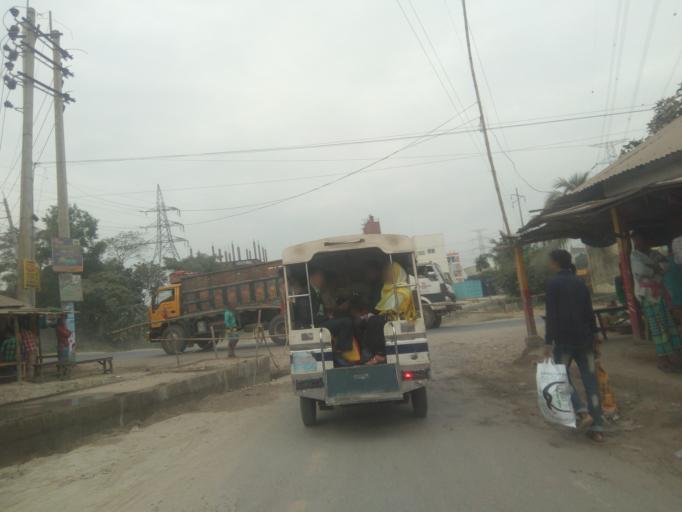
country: BD
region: Dhaka
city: Narayanganj
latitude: 23.5862
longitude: 90.5033
